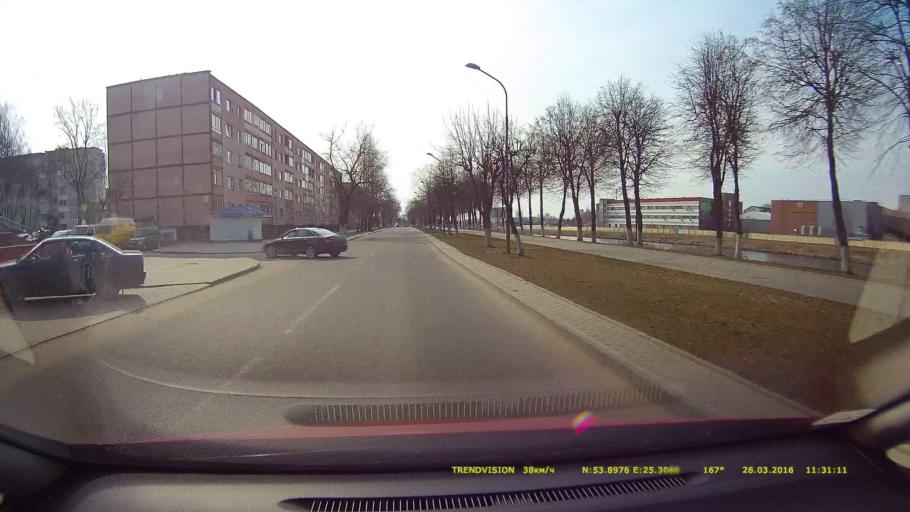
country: BY
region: Grodnenskaya
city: Lida
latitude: 53.8975
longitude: 25.3080
